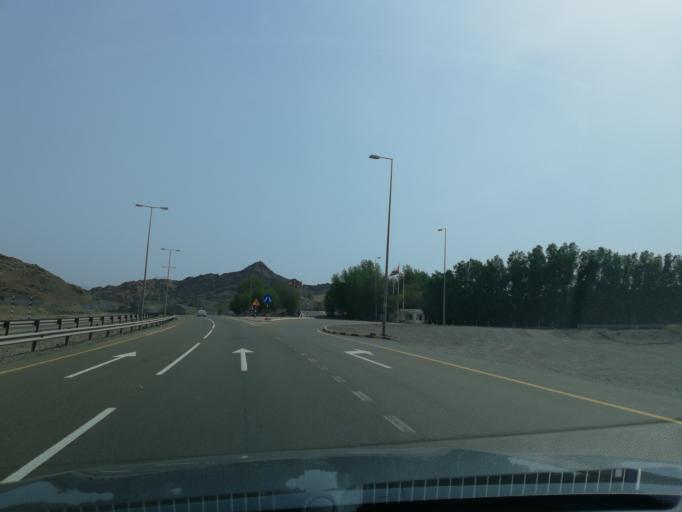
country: OM
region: Al Batinah
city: Al Liwa'
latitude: 24.3037
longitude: 56.4268
